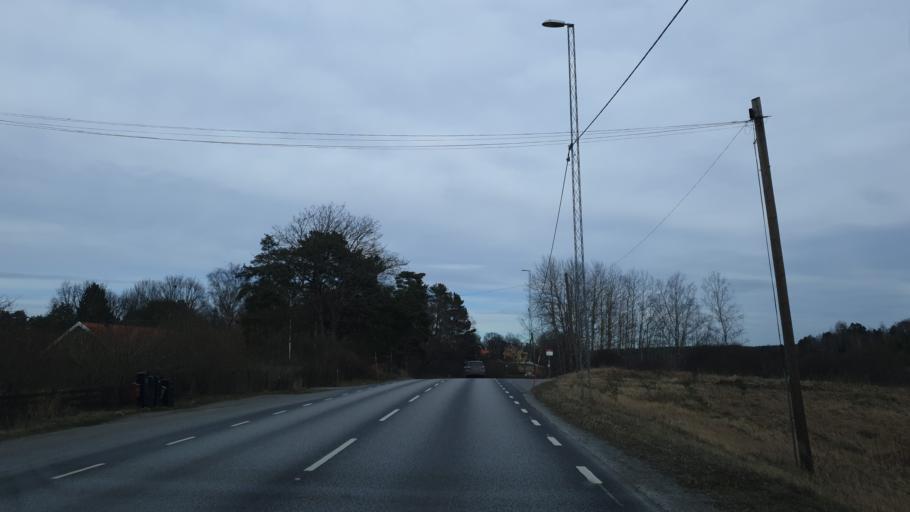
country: SE
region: Stockholm
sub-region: Osterakers Kommun
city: Akersberga
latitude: 59.5631
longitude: 18.2434
